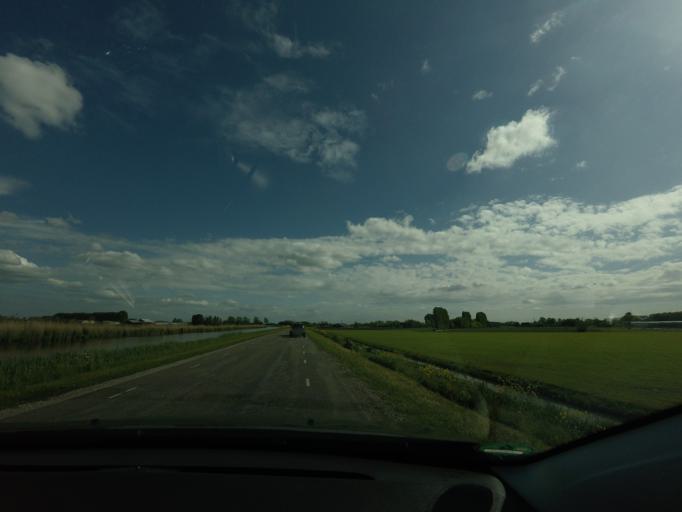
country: NL
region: North Holland
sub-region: Gemeente Heerhugowaard
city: Heerhugowaard
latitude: 52.6525
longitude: 4.8626
